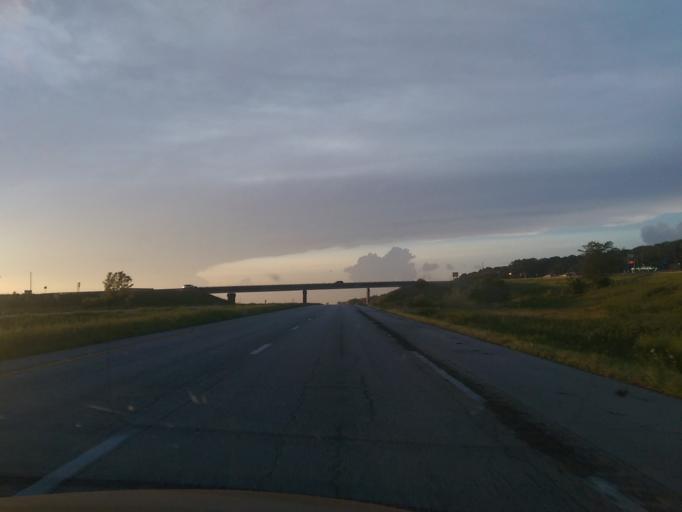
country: US
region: Missouri
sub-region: Atchison County
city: Rock Port
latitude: 40.4052
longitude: -95.5542
